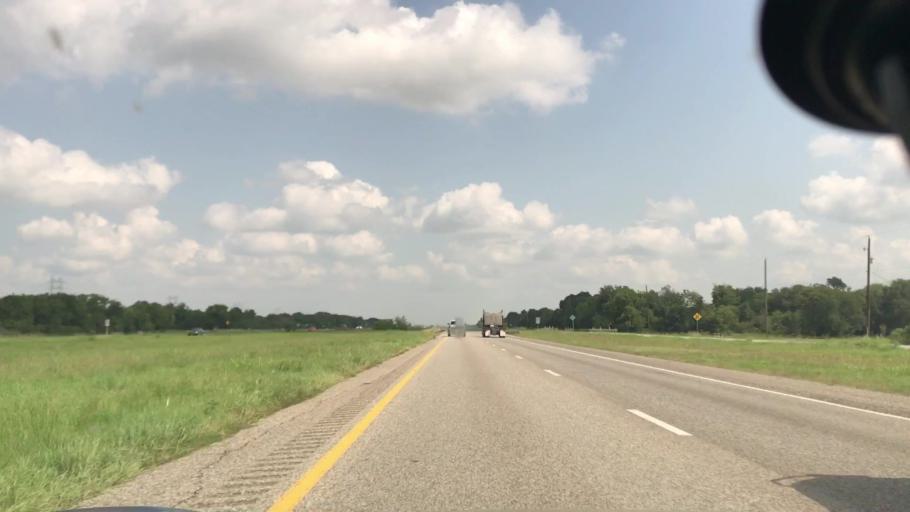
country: US
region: Texas
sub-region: Brazoria County
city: Rosharon
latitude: 29.3915
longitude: -95.4265
